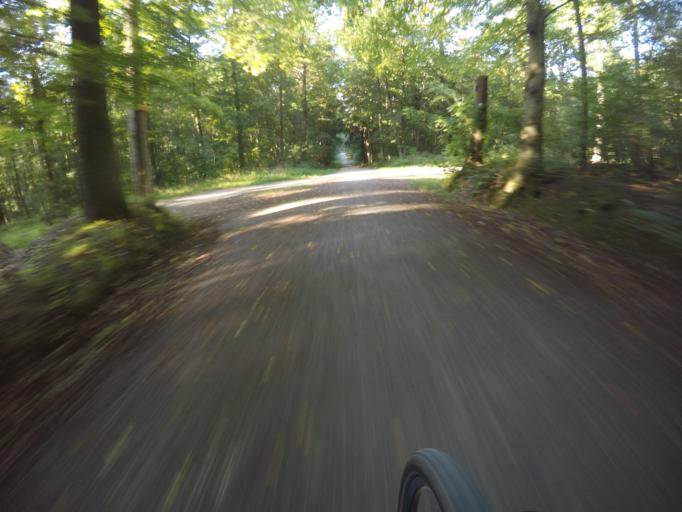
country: DE
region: Baden-Wuerttemberg
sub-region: Regierungsbezirk Stuttgart
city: Stuttgart Feuerbach
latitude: 48.8214
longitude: 9.1512
